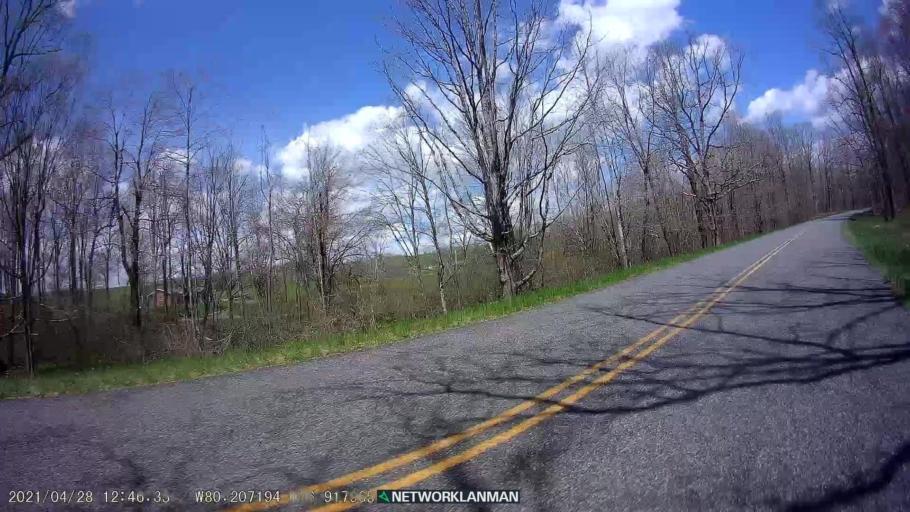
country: US
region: Virginia
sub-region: Floyd County
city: Floyd
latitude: 36.9182
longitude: -80.2071
